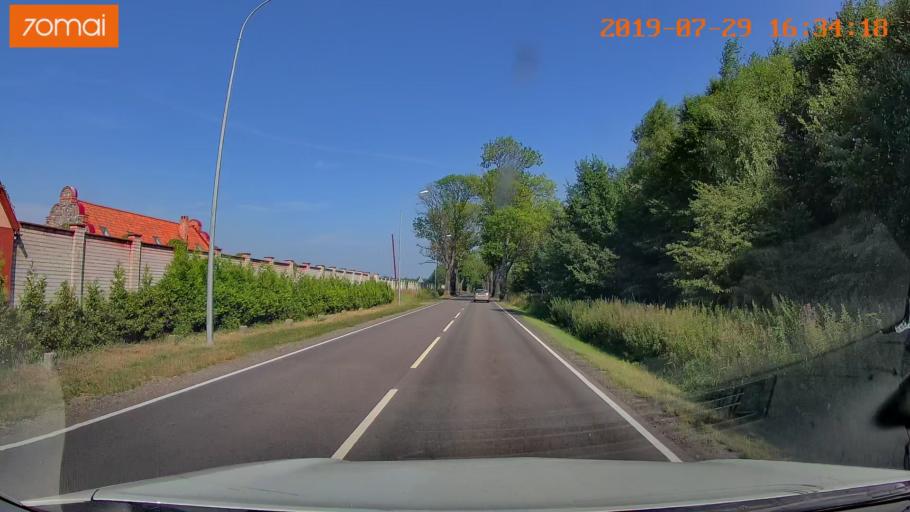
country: RU
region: Kaliningrad
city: Primorsk
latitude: 54.7398
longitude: 20.0499
